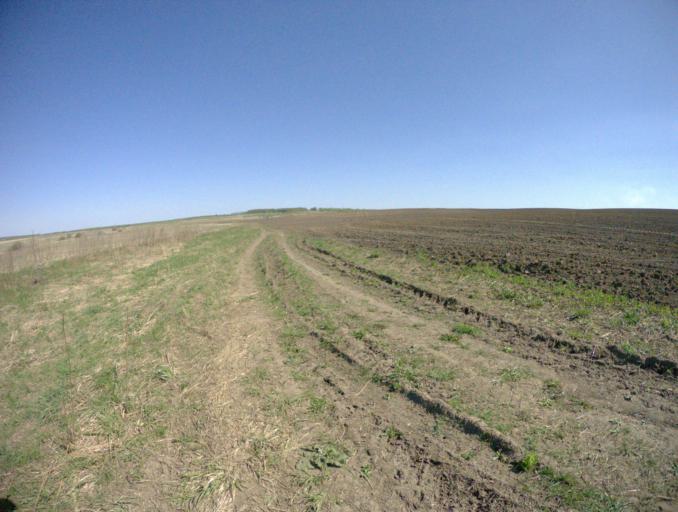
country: RU
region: Vladimir
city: Vladimir
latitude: 56.2792
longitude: 40.3466
